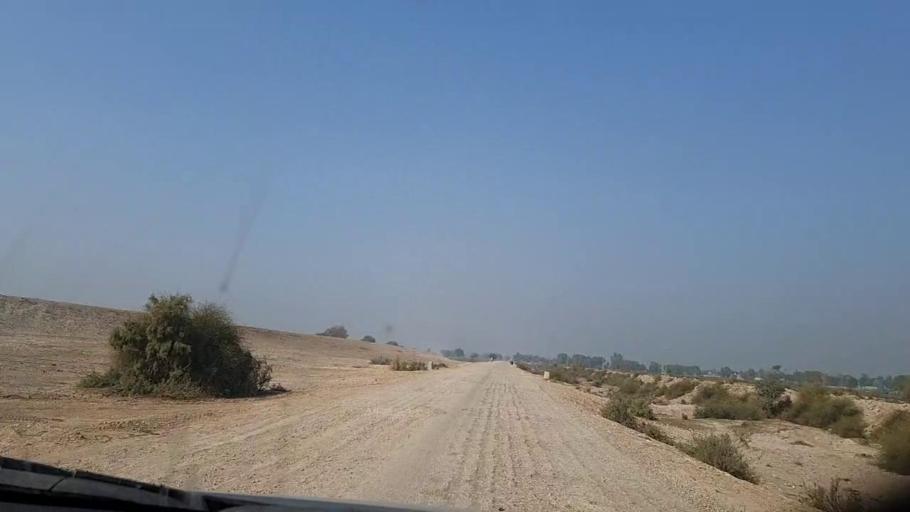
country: PK
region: Sindh
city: Moro
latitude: 26.7244
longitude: 67.9221
